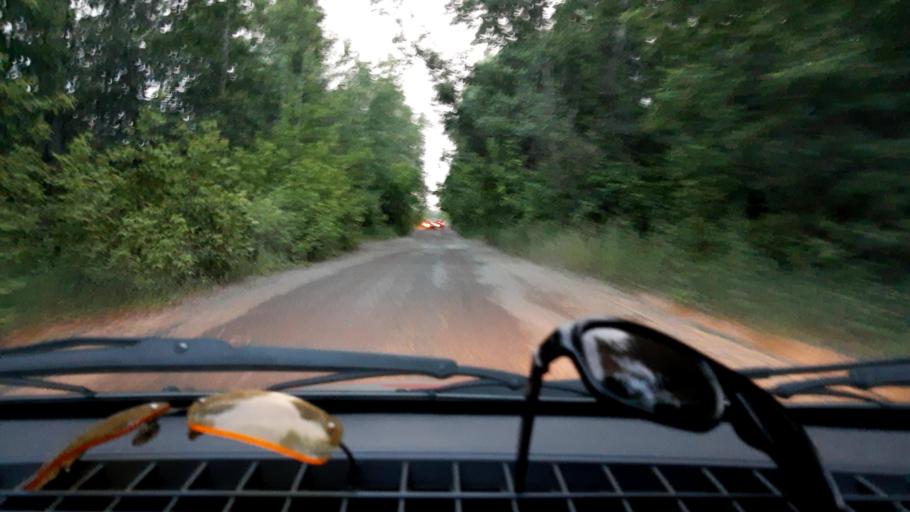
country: RU
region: Bashkortostan
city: Avdon
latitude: 54.6613
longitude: 55.8214
